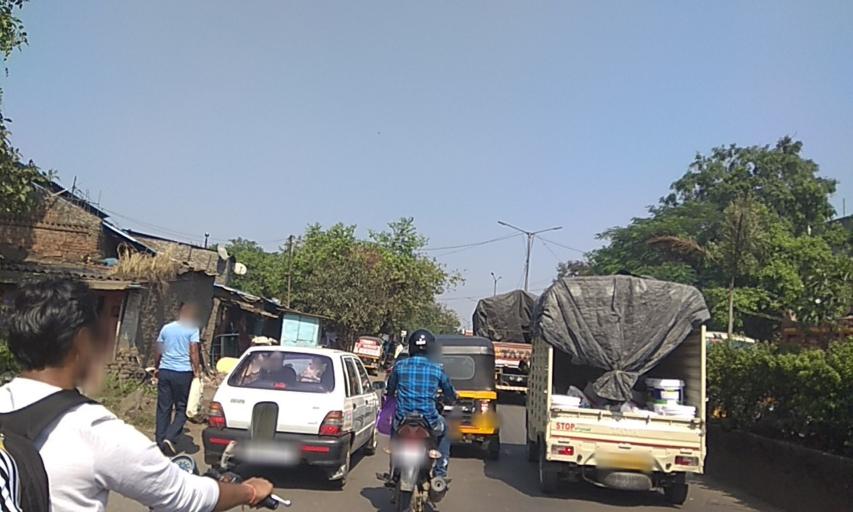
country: IN
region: Maharashtra
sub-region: Pune Division
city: Lohogaon
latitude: 18.5333
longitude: 73.9331
